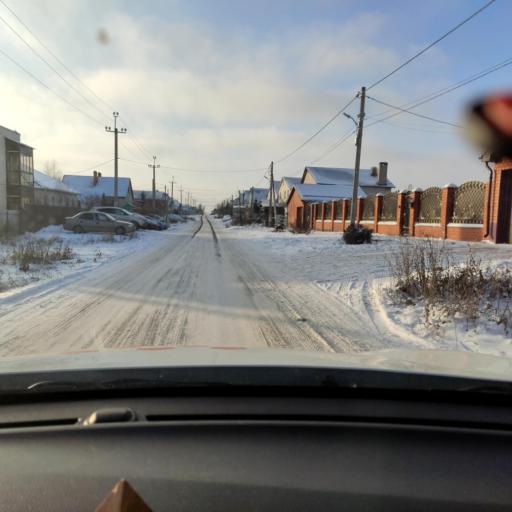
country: RU
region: Tatarstan
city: Vysokaya Gora
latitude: 55.8199
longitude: 49.2589
